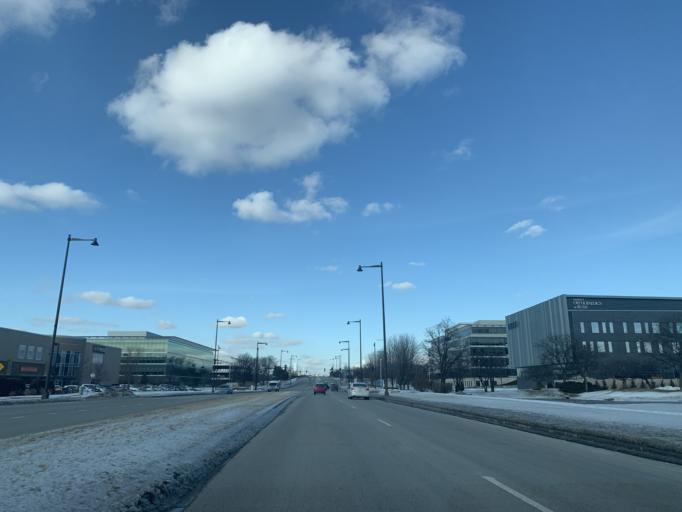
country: US
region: Illinois
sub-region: DuPage County
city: Oak Brook
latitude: 41.8483
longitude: -87.9292
